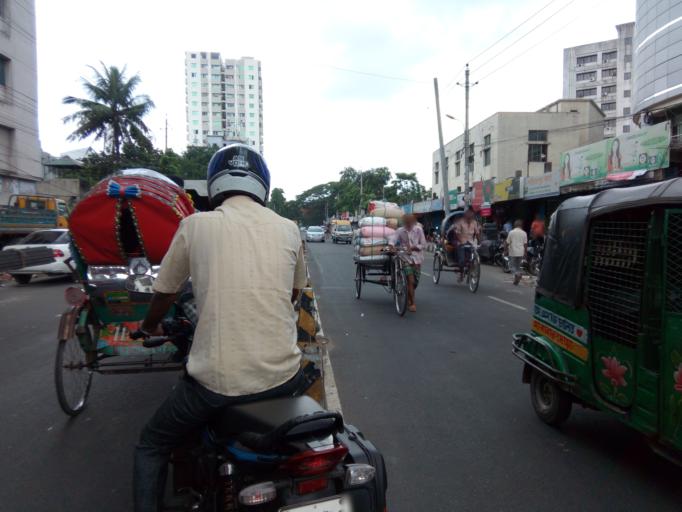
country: BD
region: Dhaka
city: Azimpur
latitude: 23.7243
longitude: 90.3974
